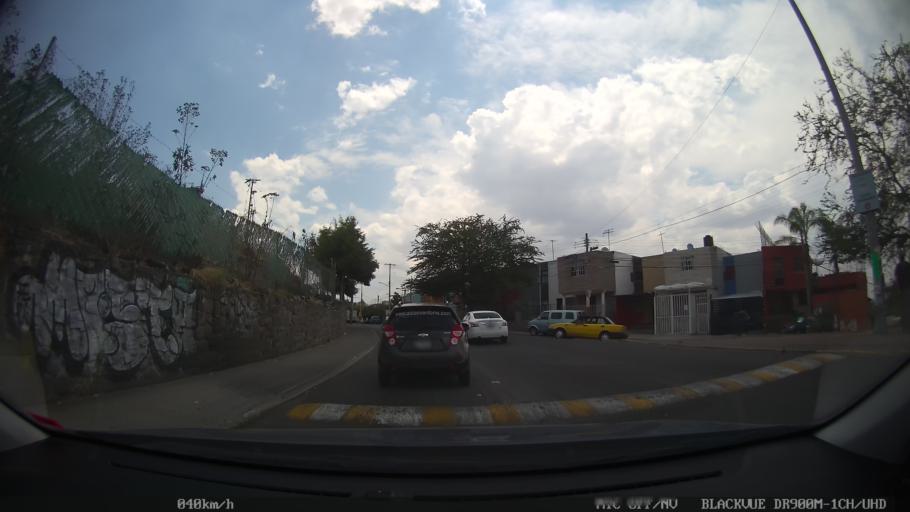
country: MX
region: Jalisco
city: Tonala
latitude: 20.6292
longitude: -103.2573
